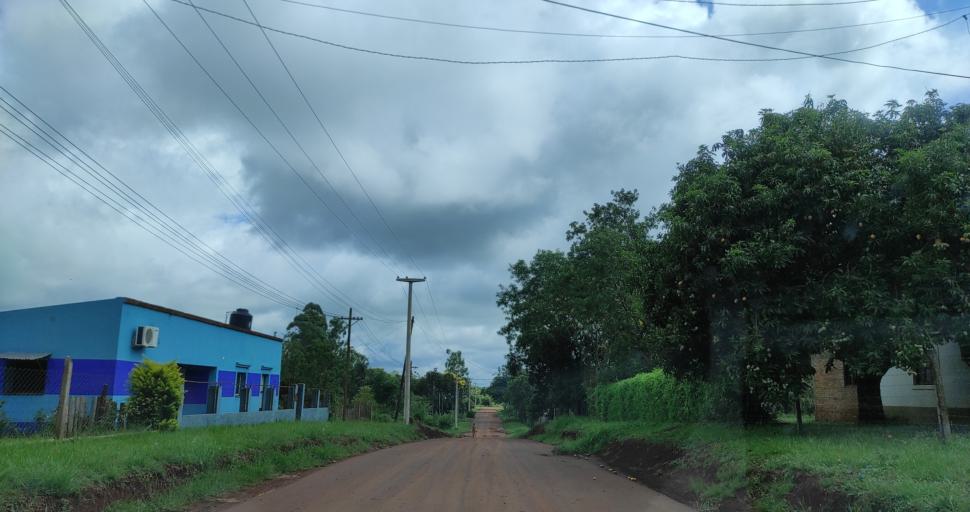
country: AR
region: Corrientes
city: San Carlos
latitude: -27.7486
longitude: -55.8915
